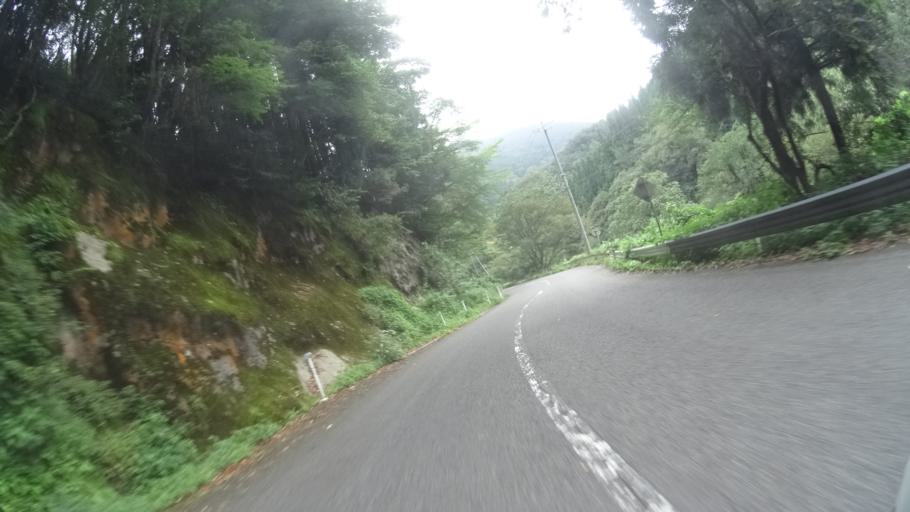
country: JP
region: Tottori
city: Kurayoshi
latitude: 35.4033
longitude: 133.9777
